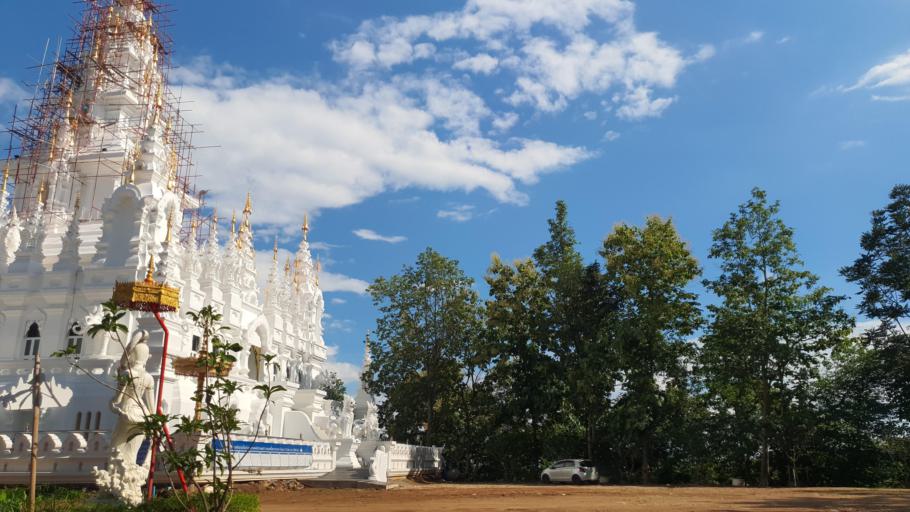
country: TH
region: Chiang Mai
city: Hang Dong
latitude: 18.7520
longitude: 98.8803
